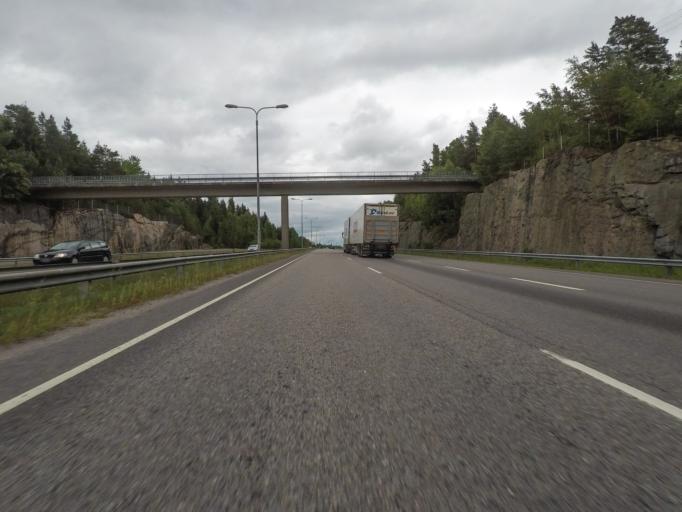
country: FI
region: Varsinais-Suomi
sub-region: Turku
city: Rusko
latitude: 60.4981
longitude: 22.2514
